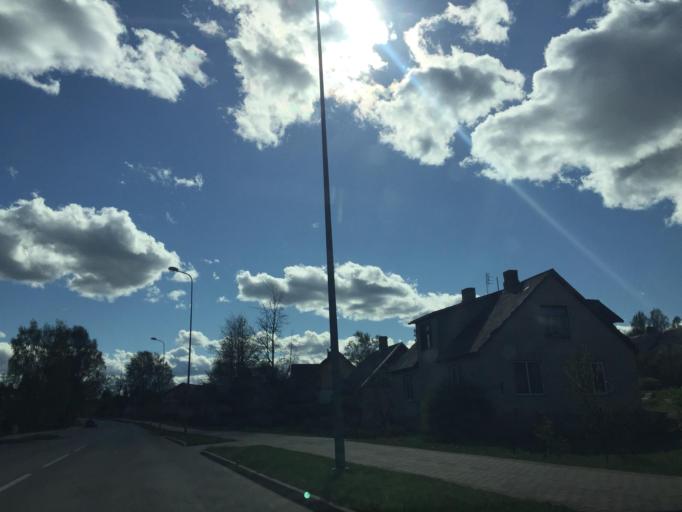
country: LV
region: Madonas Rajons
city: Madona
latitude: 56.8467
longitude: 26.2100
